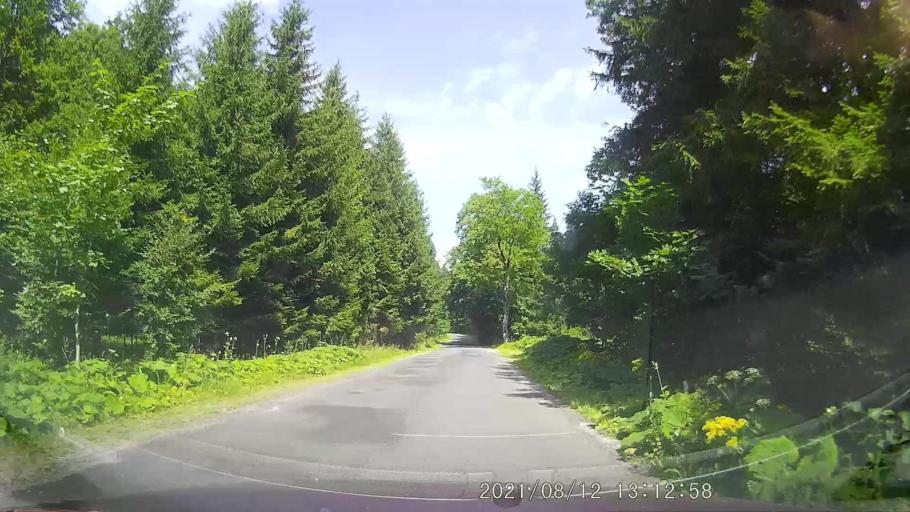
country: PL
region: Lower Silesian Voivodeship
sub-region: Powiat klodzki
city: Stronie Slaskie
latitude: 50.2506
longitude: 16.8516
